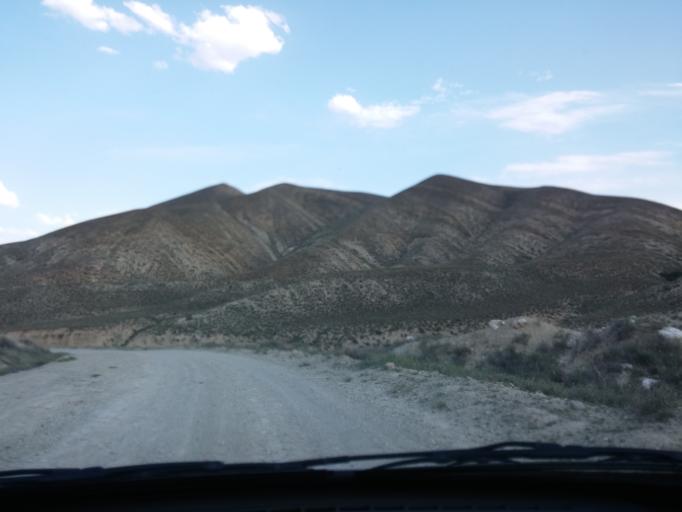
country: IR
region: Tehran
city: Damavand
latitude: 35.5331
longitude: 52.2259
